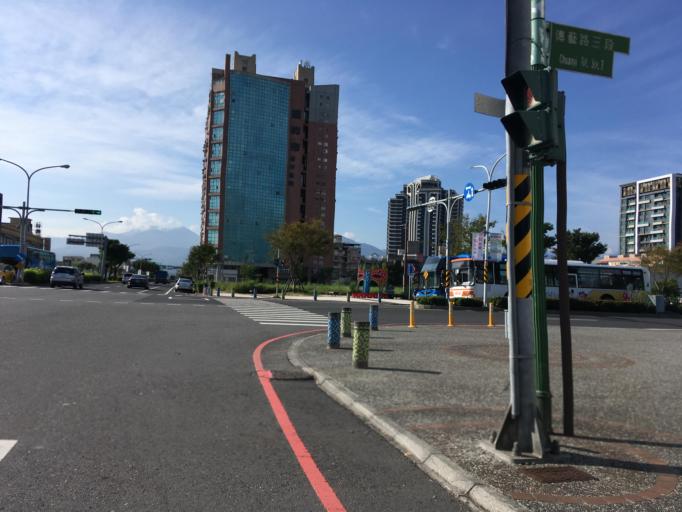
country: TW
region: Taiwan
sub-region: Yilan
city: Yilan
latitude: 24.6781
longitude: 121.7776
